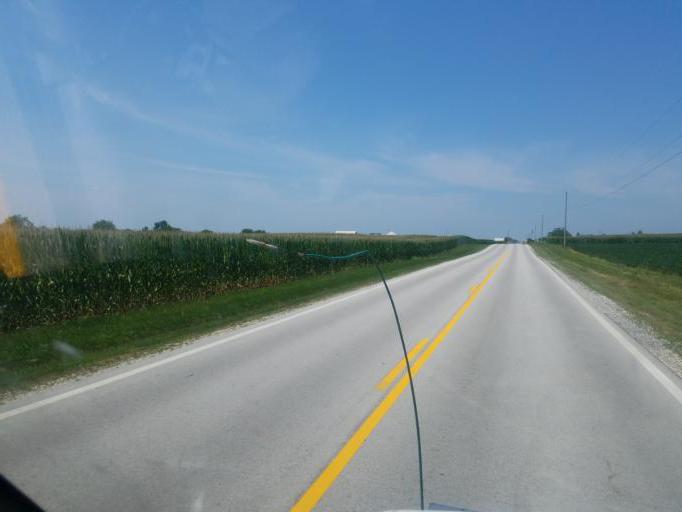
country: US
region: Ohio
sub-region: Auglaize County
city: New Bremen
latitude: 40.4317
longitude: -84.4338
